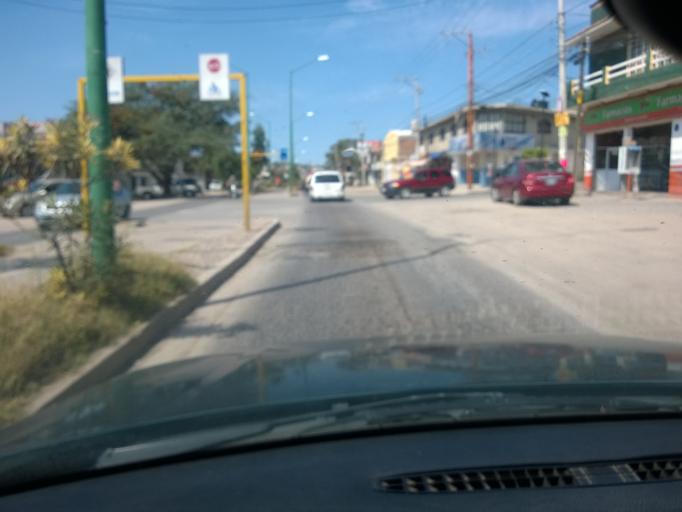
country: MX
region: Guanajuato
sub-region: Leon
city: Ejido la Joya
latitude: 21.1402
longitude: -101.7374
